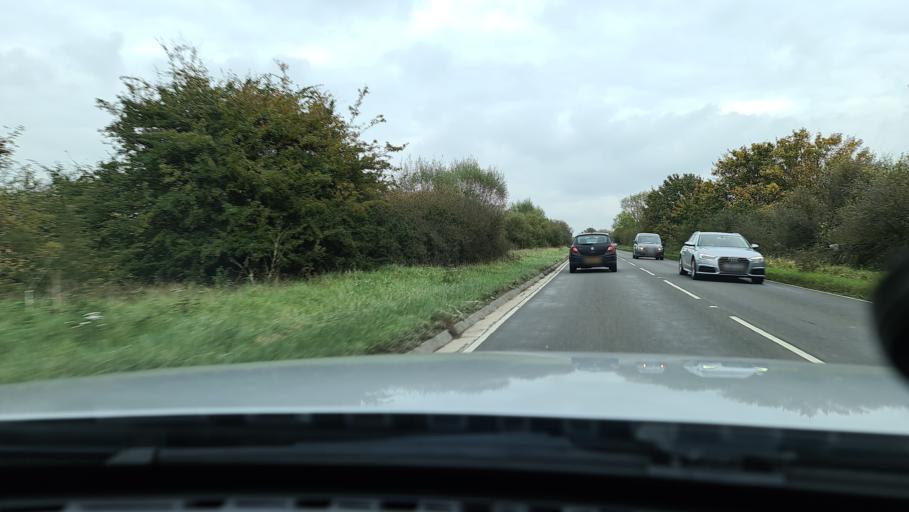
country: GB
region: England
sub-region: Oxfordshire
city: Bicester
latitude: 51.8748
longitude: -1.0757
